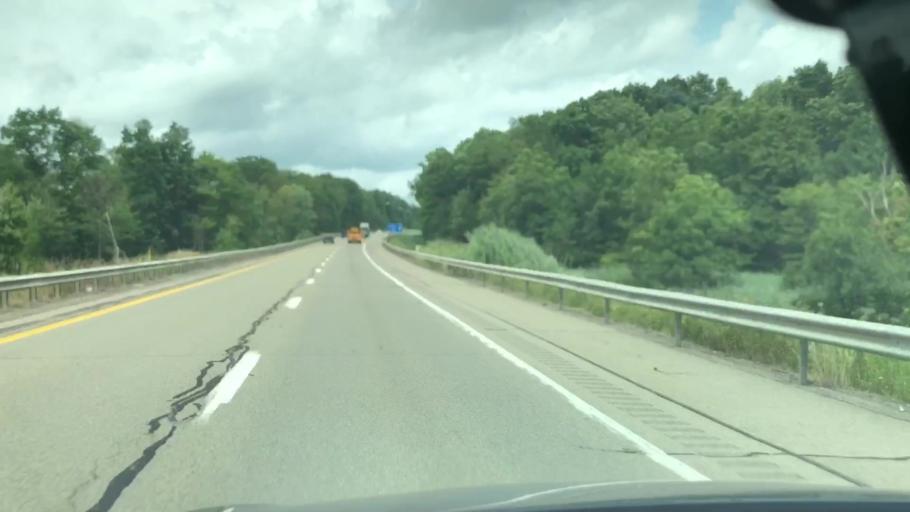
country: US
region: Pennsylvania
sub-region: Erie County
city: Edinboro
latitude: 41.8363
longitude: -80.1758
